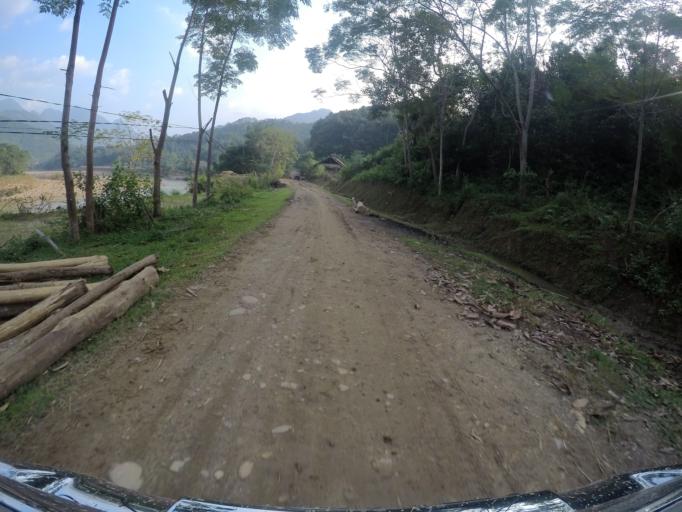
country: VN
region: Yen Bai
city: Son Thinh
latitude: 21.6851
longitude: 104.6265
